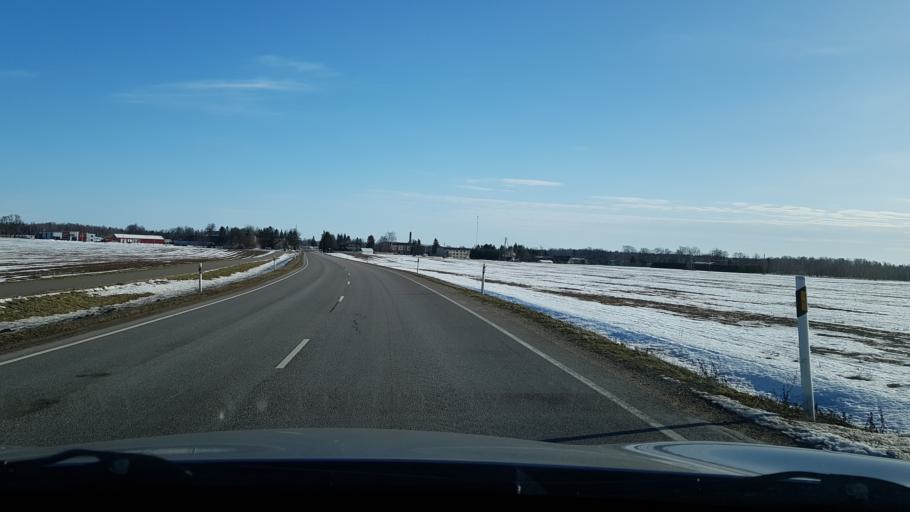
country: EE
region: Viljandimaa
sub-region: Vohma linn
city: Vohma
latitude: 58.6323
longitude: 25.7138
